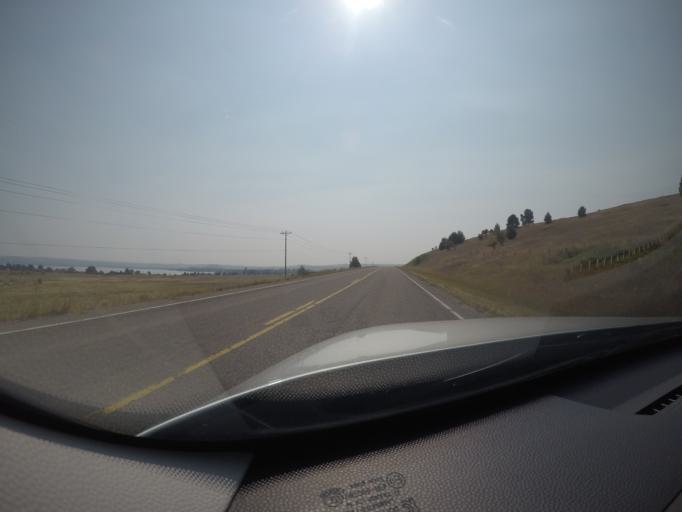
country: US
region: Montana
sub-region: Lake County
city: Polson
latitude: 47.7396
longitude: -114.1808
